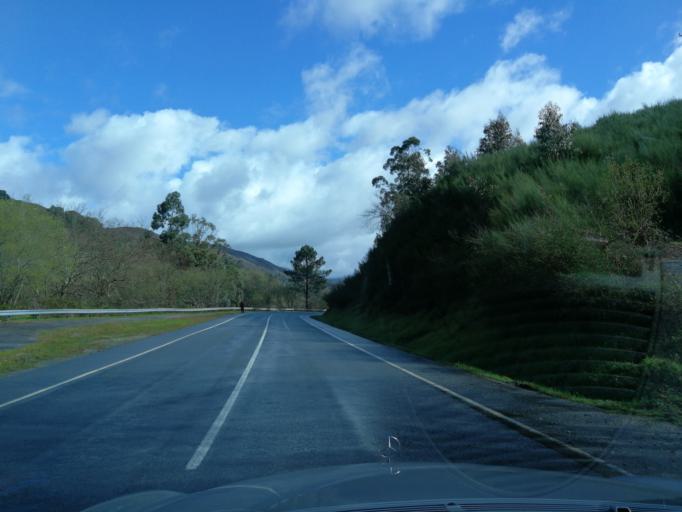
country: PT
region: Braga
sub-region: Terras de Bouro
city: Antas
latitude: 41.8280
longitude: -8.3086
